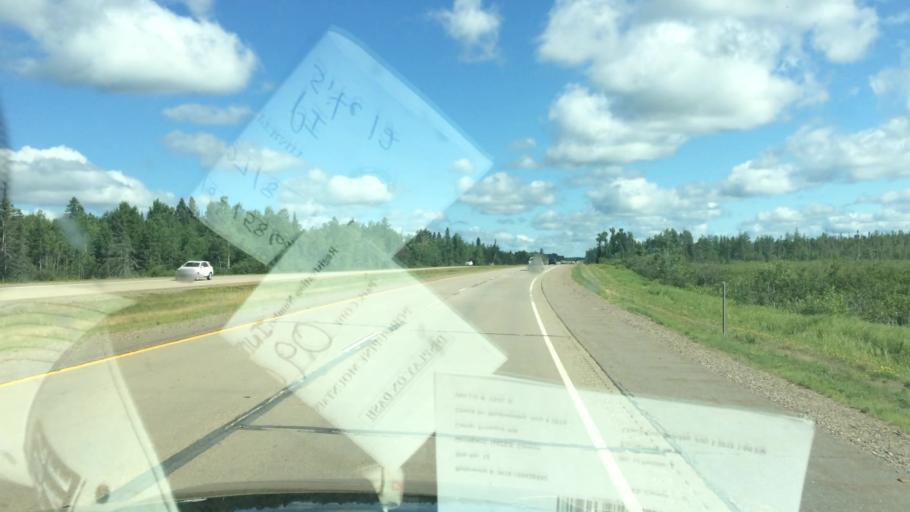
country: US
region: Wisconsin
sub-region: Lincoln County
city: Tomahawk
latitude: 45.3841
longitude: -89.6721
